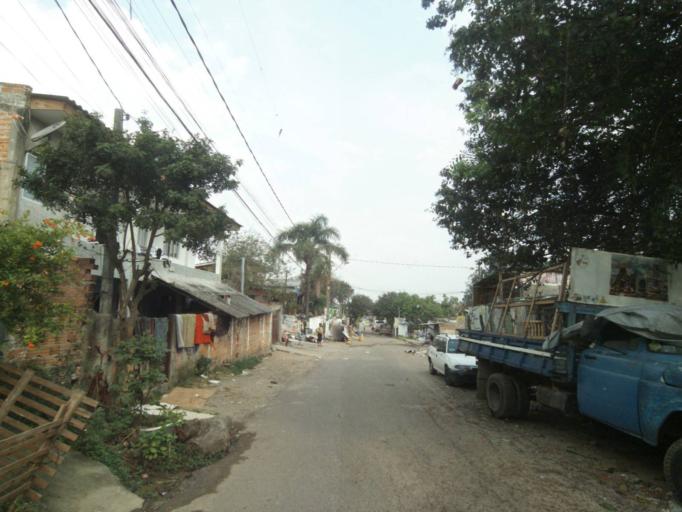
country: BR
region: Parana
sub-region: Curitiba
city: Curitiba
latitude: -25.4638
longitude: -49.2666
